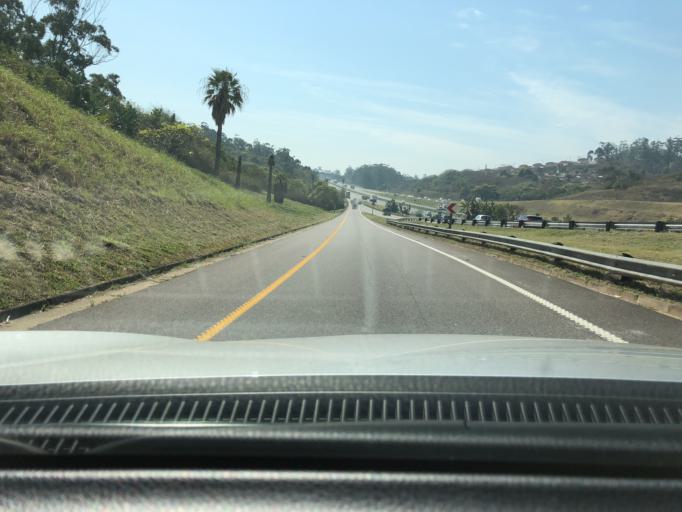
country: ZA
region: KwaZulu-Natal
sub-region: eThekwini Metropolitan Municipality
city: Berea
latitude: -29.8397
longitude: 30.9568
